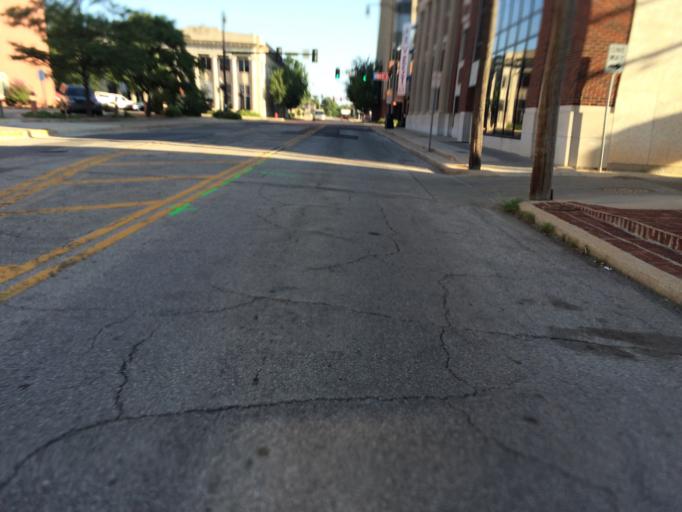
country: US
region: Oklahoma
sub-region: Cleveland County
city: Norman
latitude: 35.2210
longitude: -97.4415
